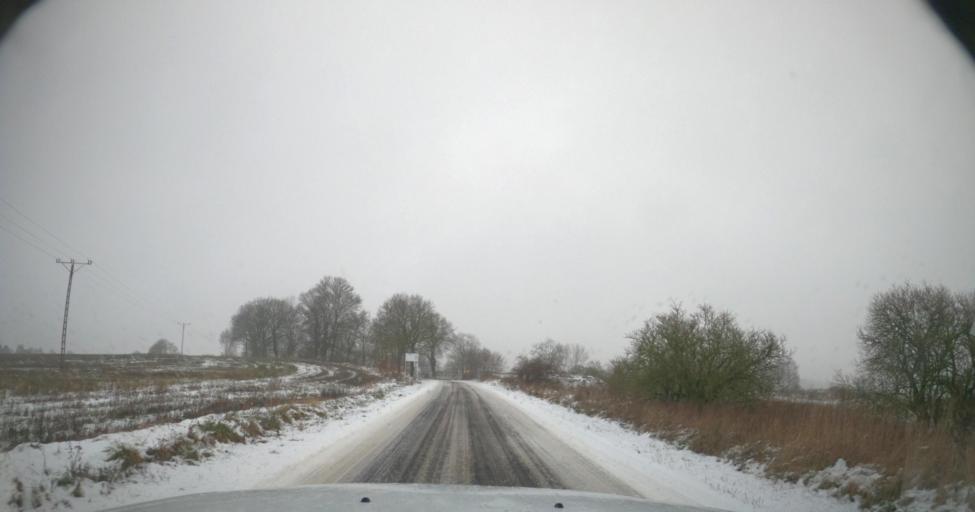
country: PL
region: West Pomeranian Voivodeship
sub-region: Powiat gryficki
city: Gryfice
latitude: 53.8914
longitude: 15.1288
